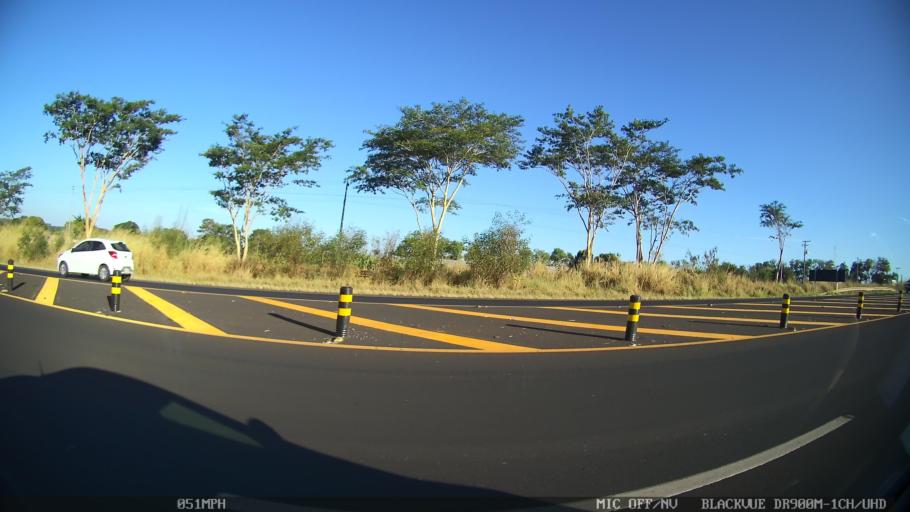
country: BR
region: Sao Paulo
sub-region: Guapiacu
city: Guapiacu
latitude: -20.7710
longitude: -49.2176
